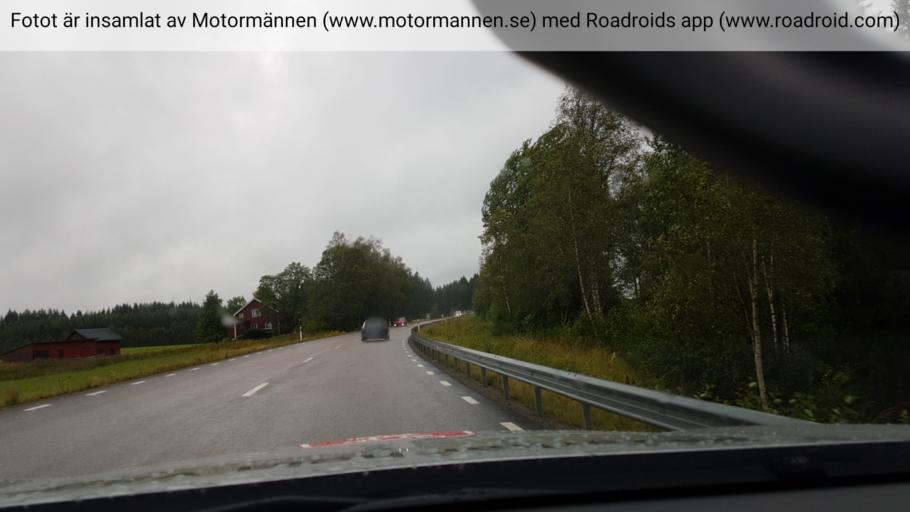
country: SE
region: Vaestra Goetaland
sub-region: Dals-Ed Kommun
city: Ed
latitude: 58.8881
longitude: 11.9158
